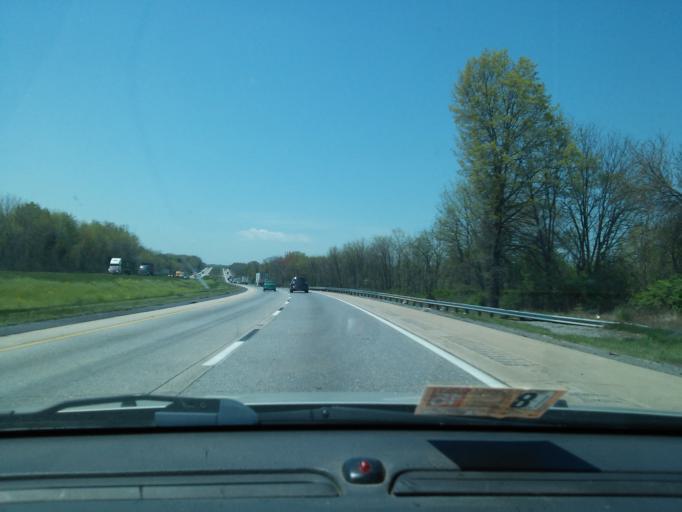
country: US
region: Pennsylvania
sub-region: Dauphin County
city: Skyline View
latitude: 40.3498
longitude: -76.7342
